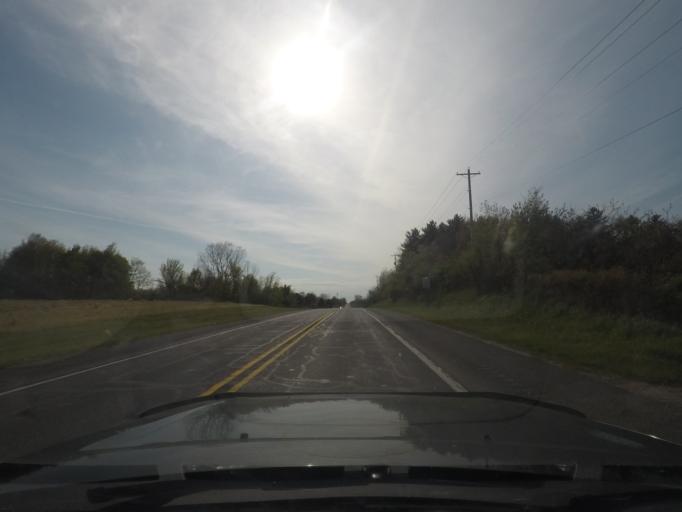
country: US
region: Indiana
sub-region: LaPorte County
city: Hudson Lake
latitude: 41.7982
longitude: -86.5099
